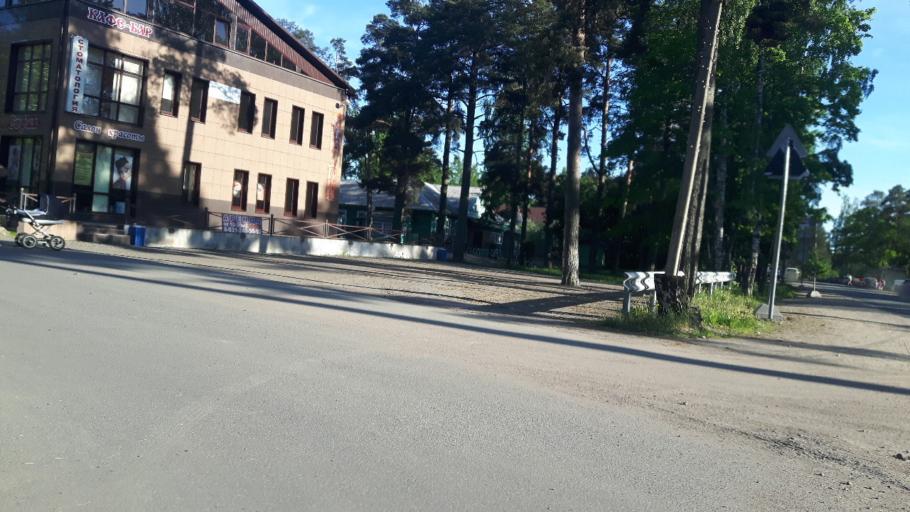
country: RU
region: Leningrad
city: Vistino
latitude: 59.7708
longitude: 28.4743
